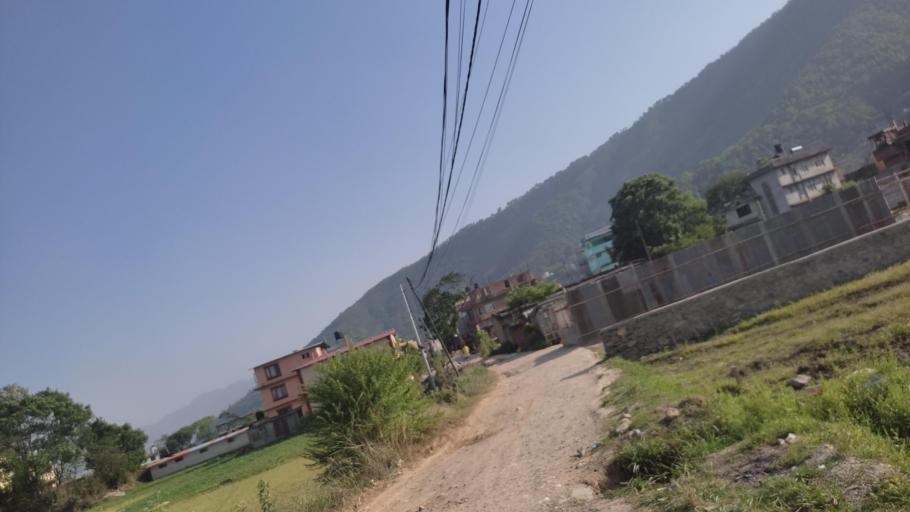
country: NP
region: Central Region
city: Kirtipur
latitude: 27.6535
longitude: 85.2797
